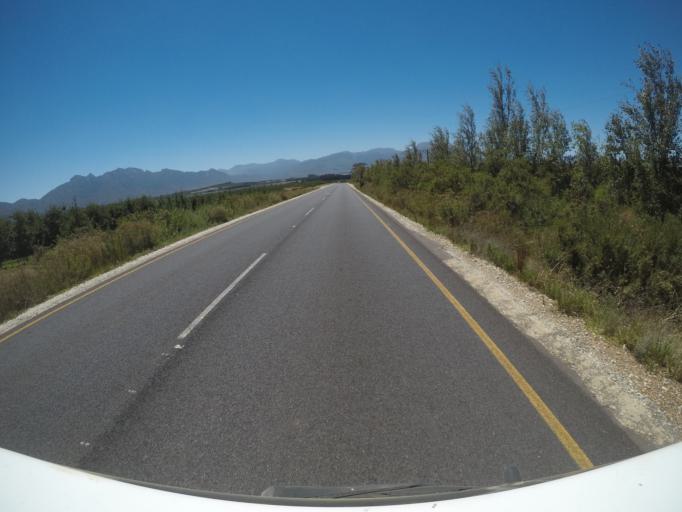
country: ZA
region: Western Cape
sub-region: Overberg District Municipality
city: Grabouw
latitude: -34.0626
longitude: 19.1349
